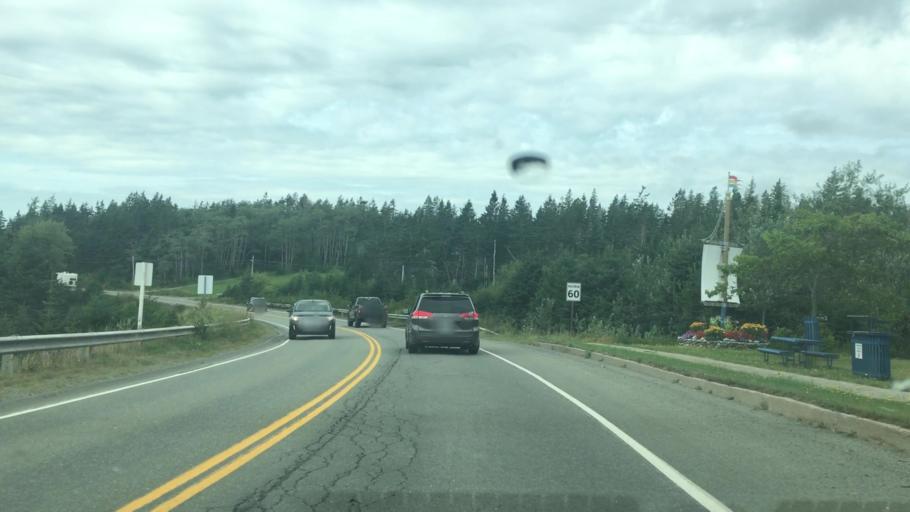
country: CA
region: Nova Scotia
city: Princeville
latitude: 45.6557
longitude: -60.8958
